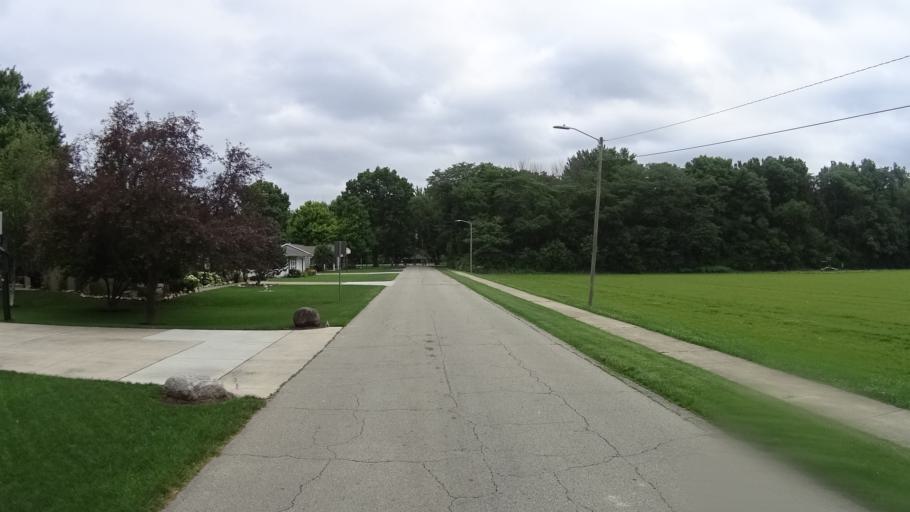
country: US
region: Indiana
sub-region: Madison County
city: Pendleton
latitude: 40.0051
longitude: -85.7416
